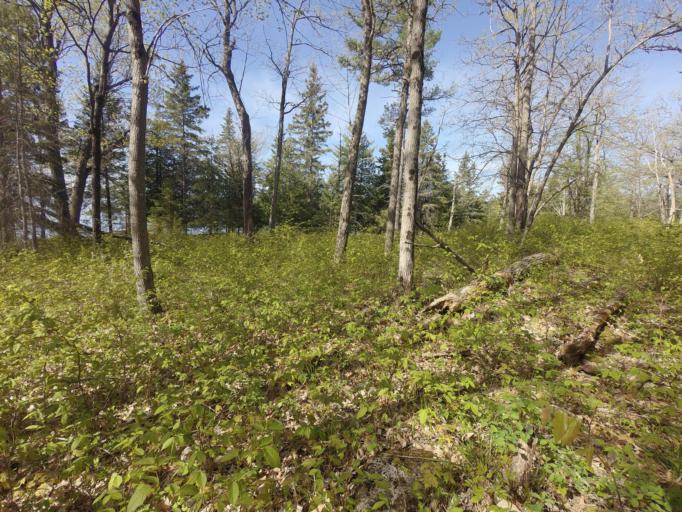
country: CA
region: Ontario
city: Arnprior
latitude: 45.4695
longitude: -76.2968
